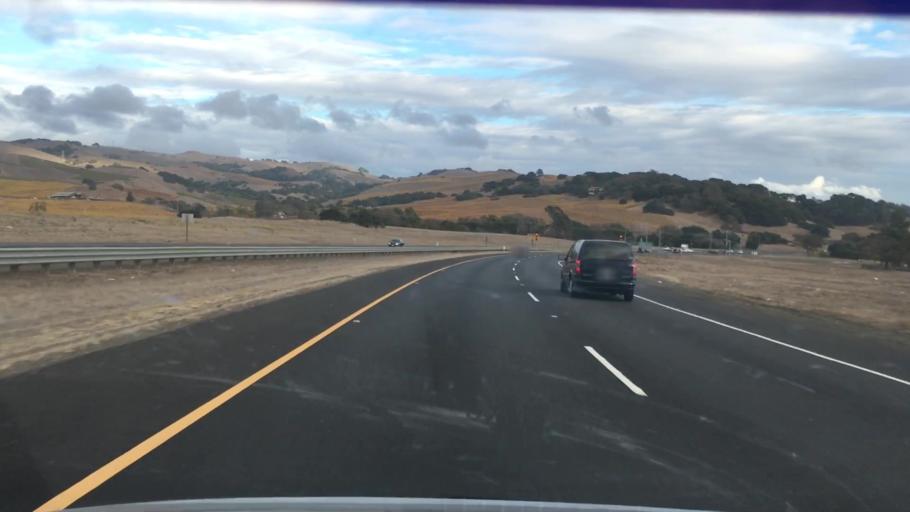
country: US
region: California
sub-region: Napa County
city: Napa
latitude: 38.2429
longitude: -122.2739
